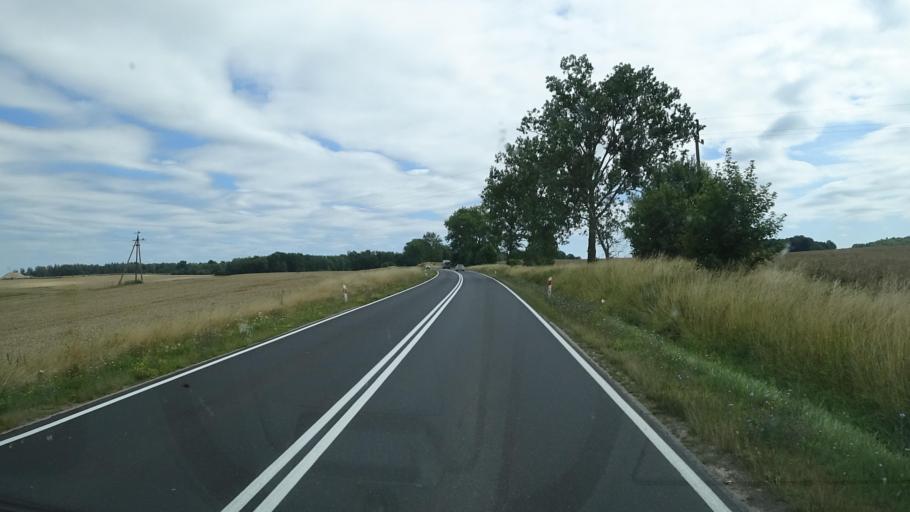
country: PL
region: Warmian-Masurian Voivodeship
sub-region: Powiat elcki
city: Stare Juchy
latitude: 53.7926
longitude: 22.2095
